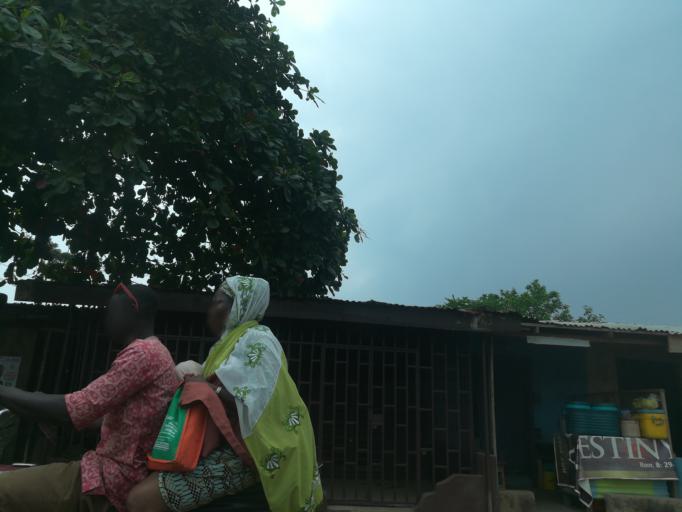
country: NG
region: Lagos
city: Ikorodu
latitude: 6.5722
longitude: 3.5920
